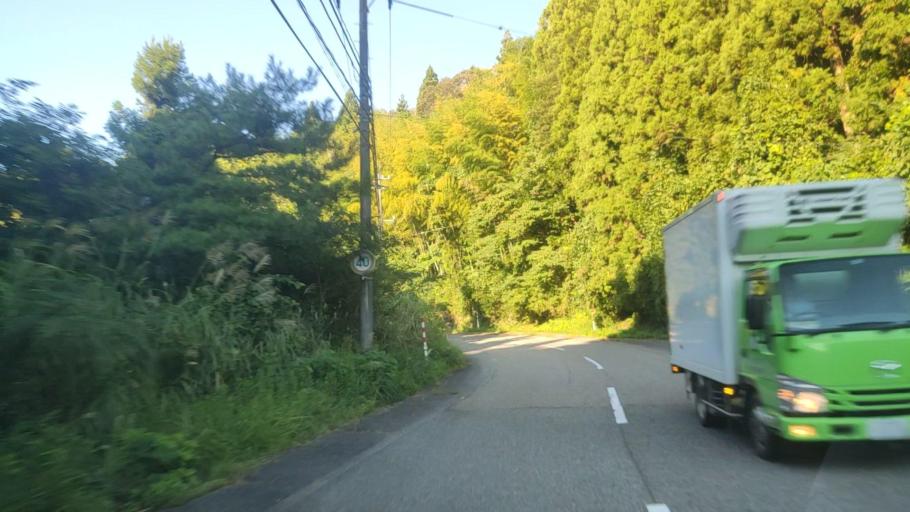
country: JP
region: Ishikawa
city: Nanao
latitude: 37.1146
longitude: 136.9656
